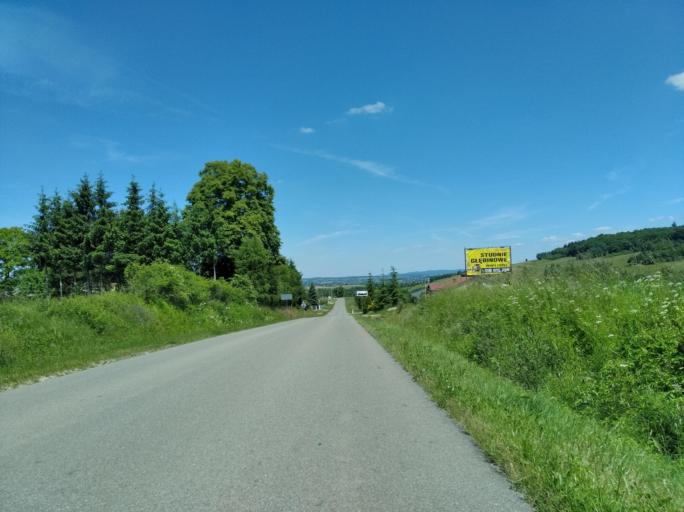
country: PL
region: Subcarpathian Voivodeship
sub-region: Powiat jasielski
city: Tarnowiec
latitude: 49.6784
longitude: 21.5423
